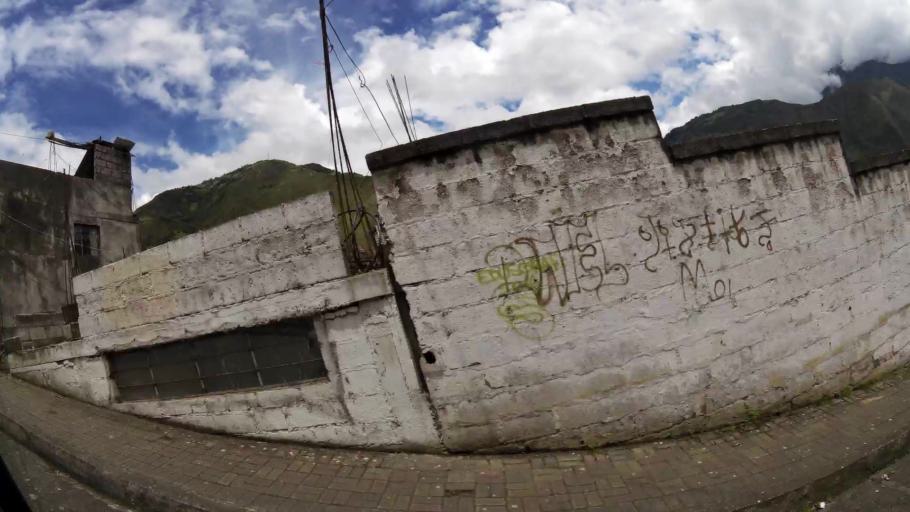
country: EC
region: Tungurahua
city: Banos
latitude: -1.3985
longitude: -78.4266
